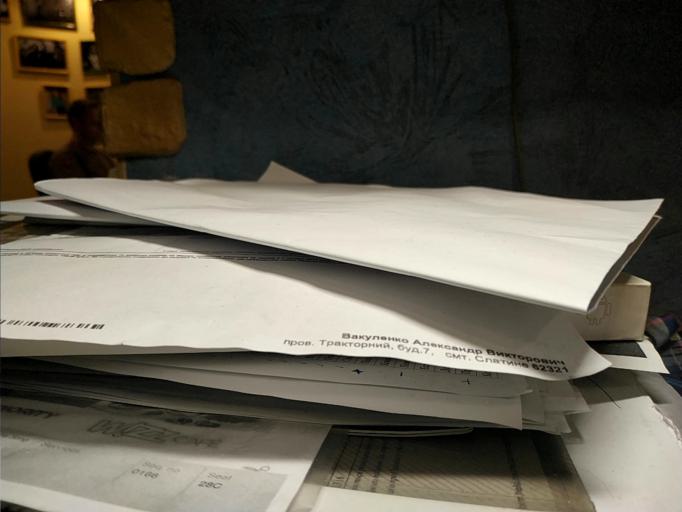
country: RU
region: Tverskaya
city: Zubtsov
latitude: 56.1127
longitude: 34.6164
